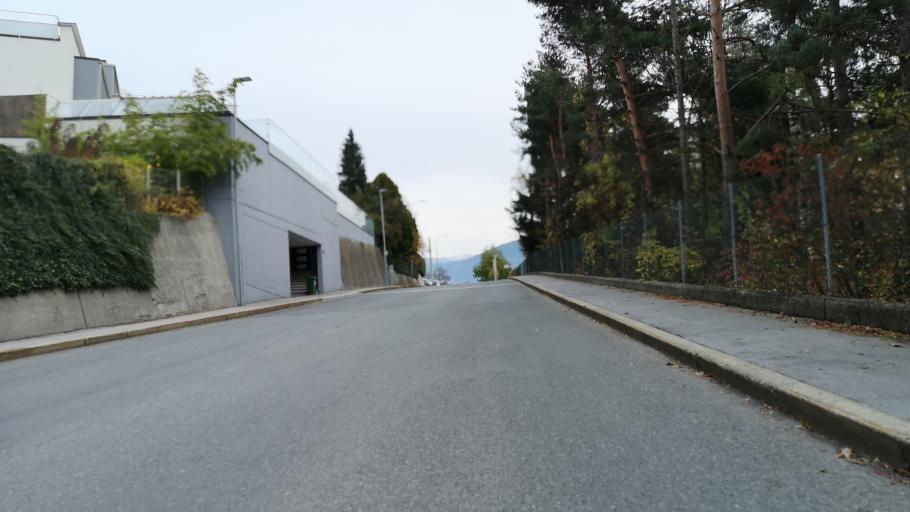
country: AT
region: Tyrol
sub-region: Politischer Bezirk Innsbruck Land
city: Vols
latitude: 47.2675
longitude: 11.3496
